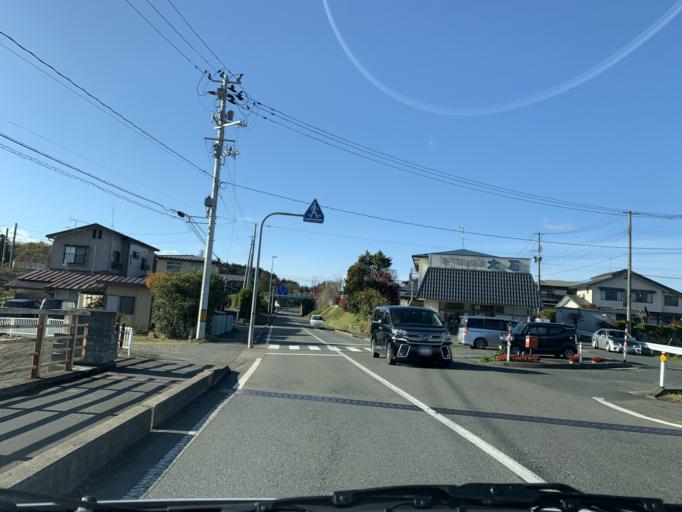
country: JP
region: Iwate
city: Mizusawa
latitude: 39.2050
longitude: 141.1116
